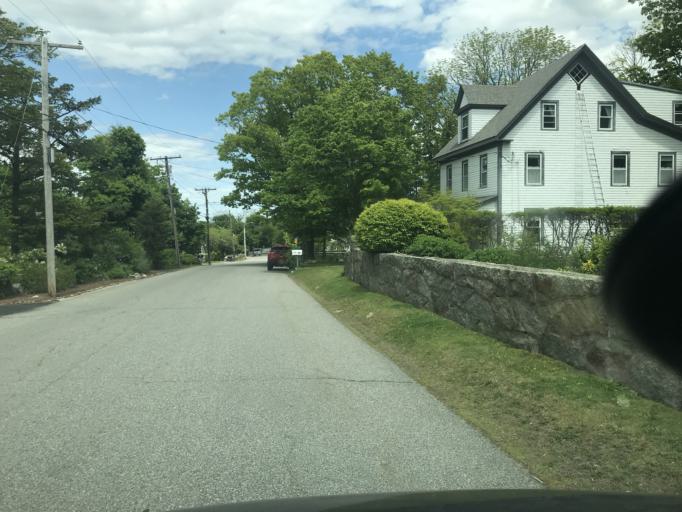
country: US
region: Massachusetts
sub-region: Essex County
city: Rockport
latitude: 42.6568
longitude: -70.6037
